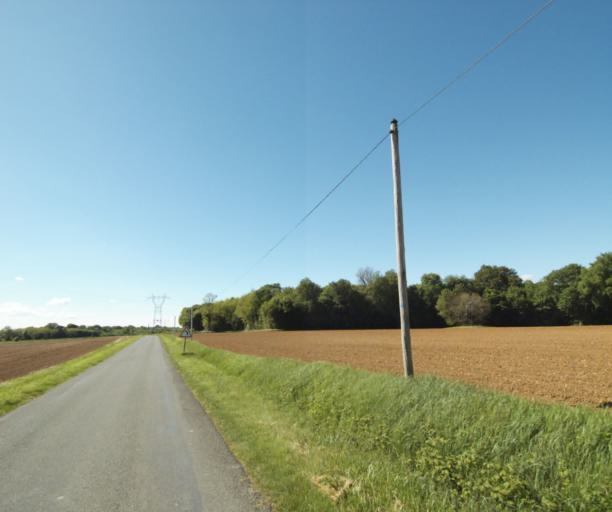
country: FR
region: Poitou-Charentes
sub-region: Departement de la Charente-Maritime
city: Saint-Georges-des-Coteaux
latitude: 45.7978
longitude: -0.6811
